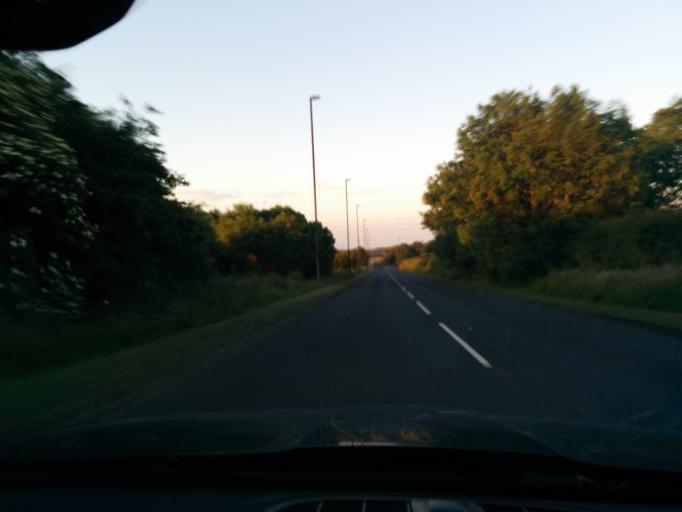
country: GB
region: England
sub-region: Northumberland
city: Seghill
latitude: 55.0443
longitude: -1.5570
